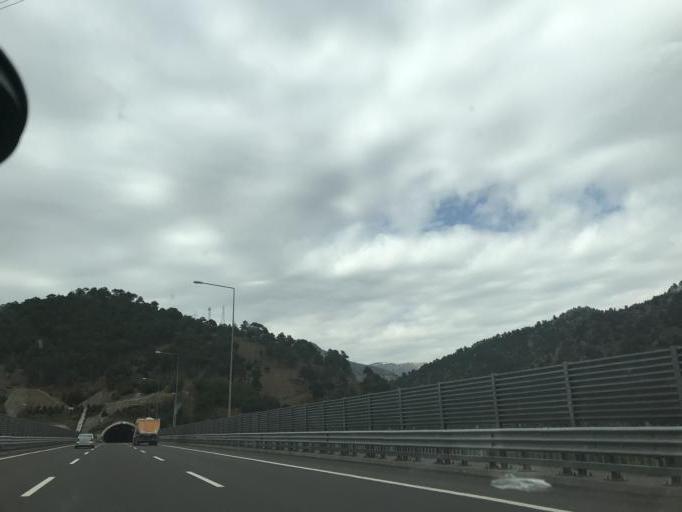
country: TR
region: Nigde
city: Ciftehan
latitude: 37.5063
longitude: 34.8207
